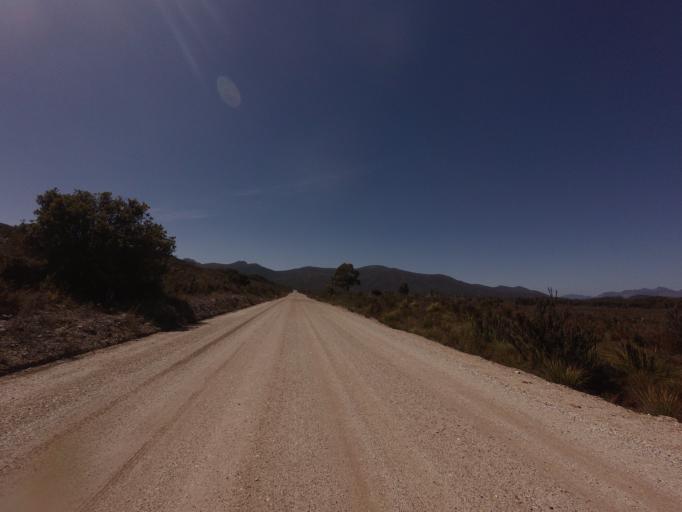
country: AU
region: Tasmania
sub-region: Huon Valley
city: Geeveston
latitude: -43.0362
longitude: 146.3209
